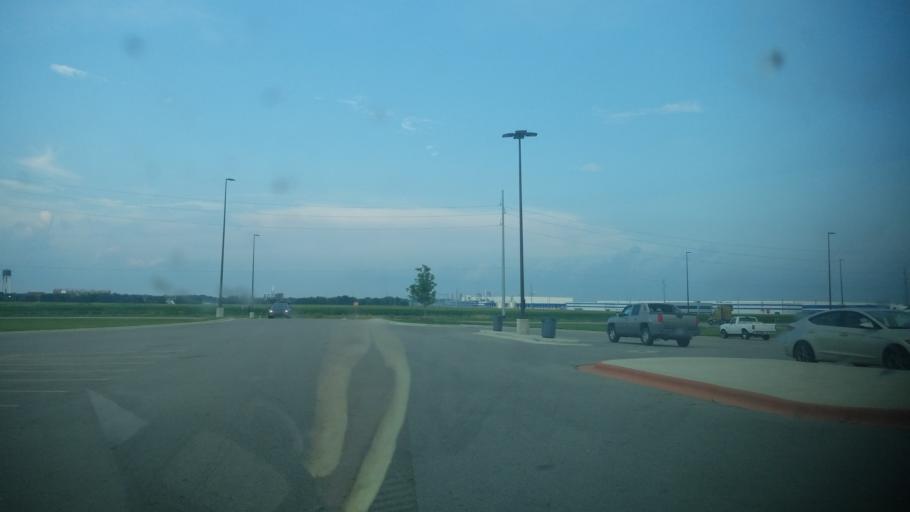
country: US
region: Ohio
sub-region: Pickaway County
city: Logan Elm Village
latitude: 39.5567
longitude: -82.9571
